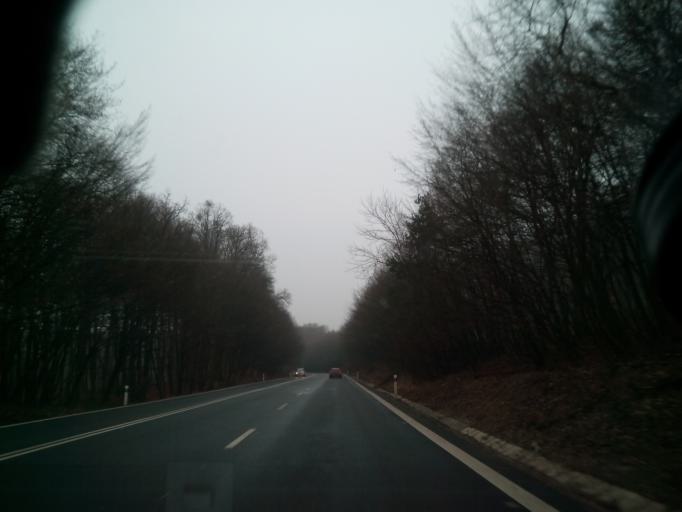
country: SK
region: Kosicky
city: Kosice
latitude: 48.7342
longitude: 21.3803
